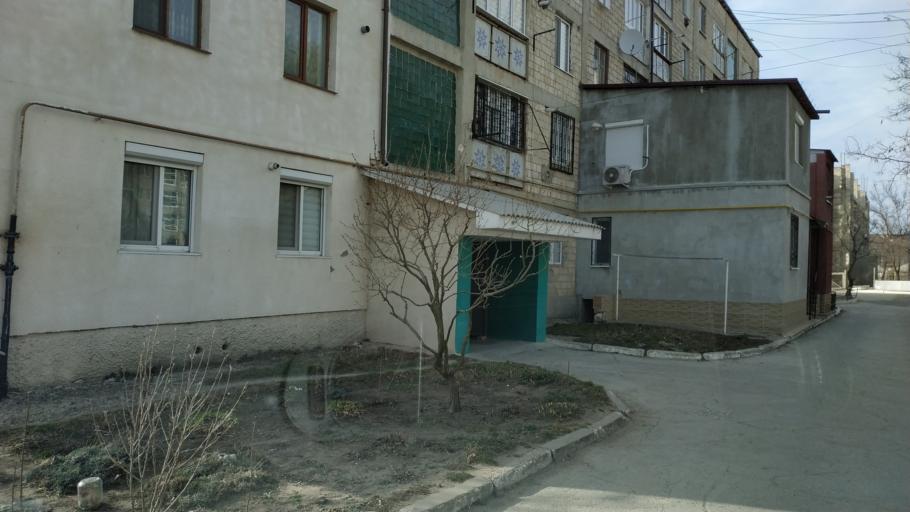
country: MD
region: Laloveni
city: Ialoveni
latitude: 46.9393
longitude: 28.7804
